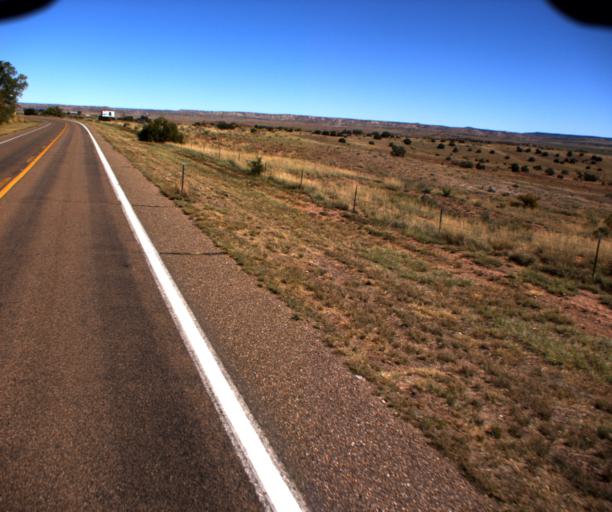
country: US
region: Arizona
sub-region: Apache County
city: Saint Johns
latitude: 34.4901
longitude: -109.3737
